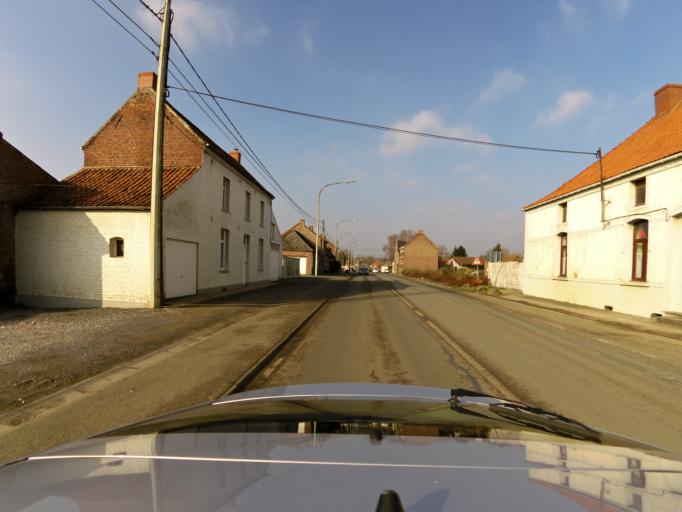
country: BE
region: Wallonia
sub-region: Province du Hainaut
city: Boussu
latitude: 50.4787
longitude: 3.7680
